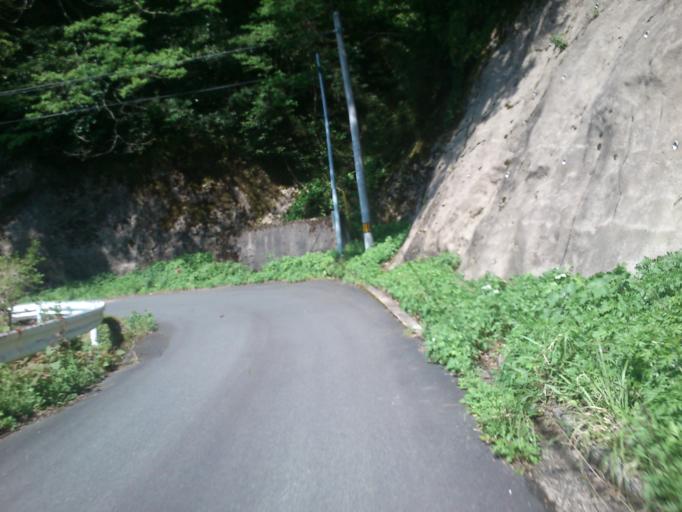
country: JP
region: Kyoto
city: Miyazu
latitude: 35.7021
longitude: 135.1564
